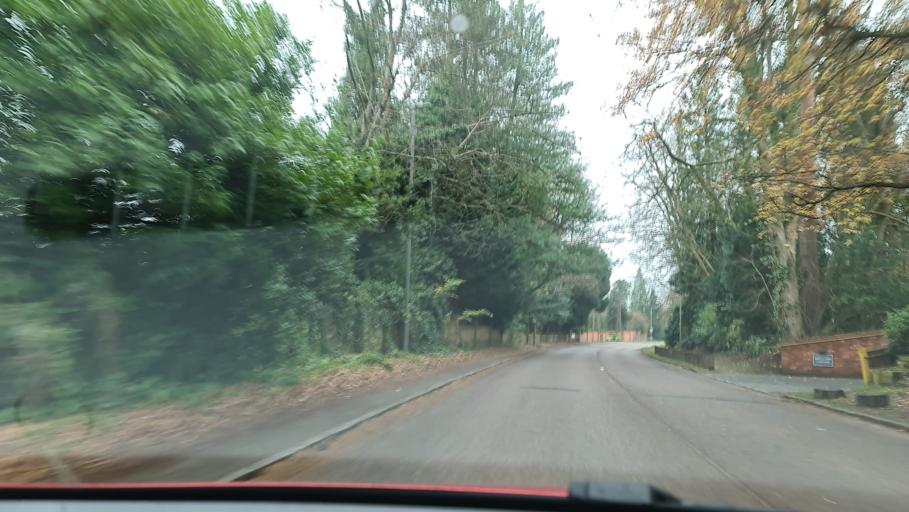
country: GB
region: England
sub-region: Buckinghamshire
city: Beaconsfield
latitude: 51.6209
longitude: -0.6519
